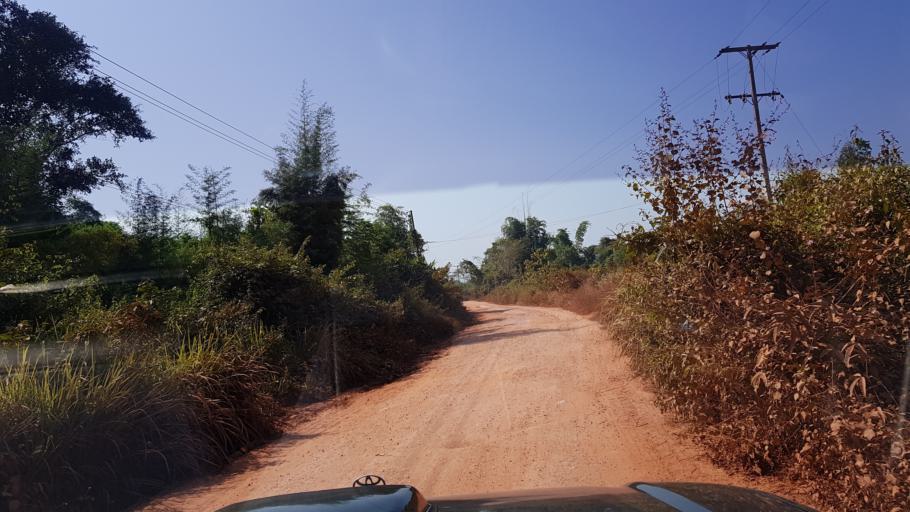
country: LA
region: Oudomxai
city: Muang Xay
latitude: 20.7147
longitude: 102.0382
